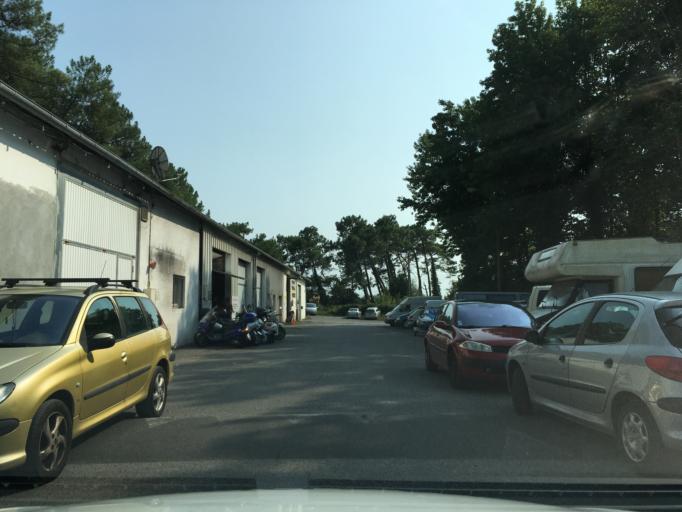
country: FR
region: Aquitaine
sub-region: Departement des Pyrenees-Atlantiques
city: Bayonne
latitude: 43.5149
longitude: -1.4981
